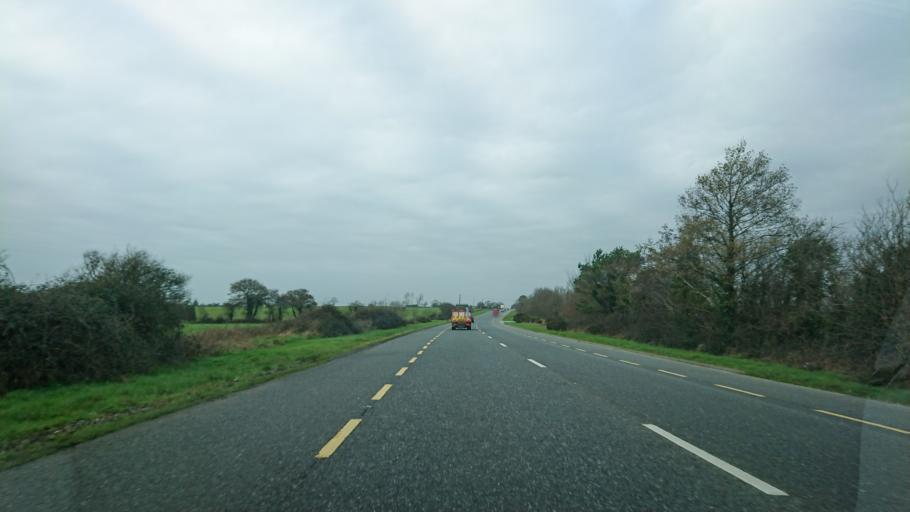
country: IE
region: Munster
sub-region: County Cork
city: Youghal
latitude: 51.9381
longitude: -7.9404
